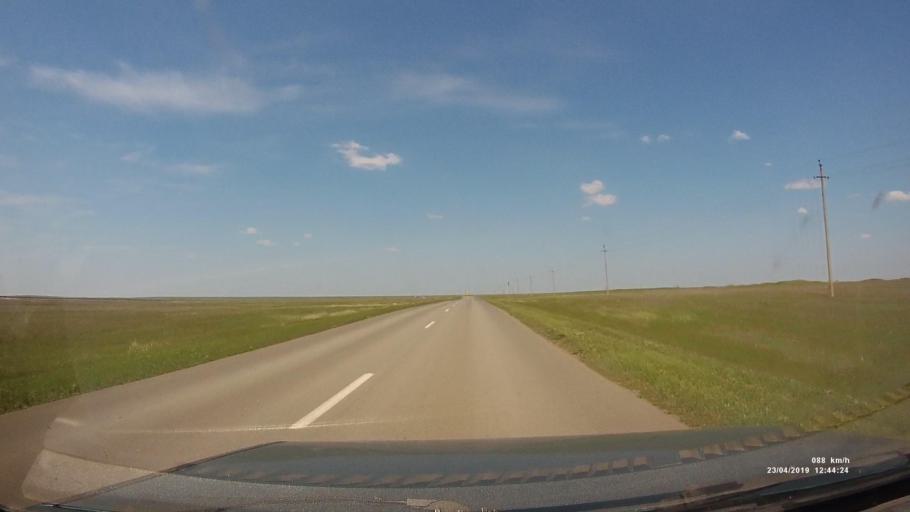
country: RU
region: Kalmykiya
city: Yashalta
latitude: 46.4764
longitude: 42.6477
